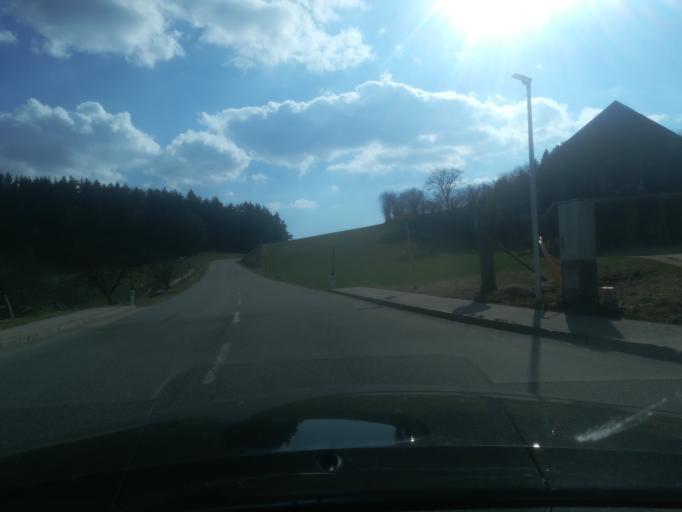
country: AT
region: Upper Austria
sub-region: Politischer Bezirk Freistadt
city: Freistadt
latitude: 48.4575
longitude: 14.7024
